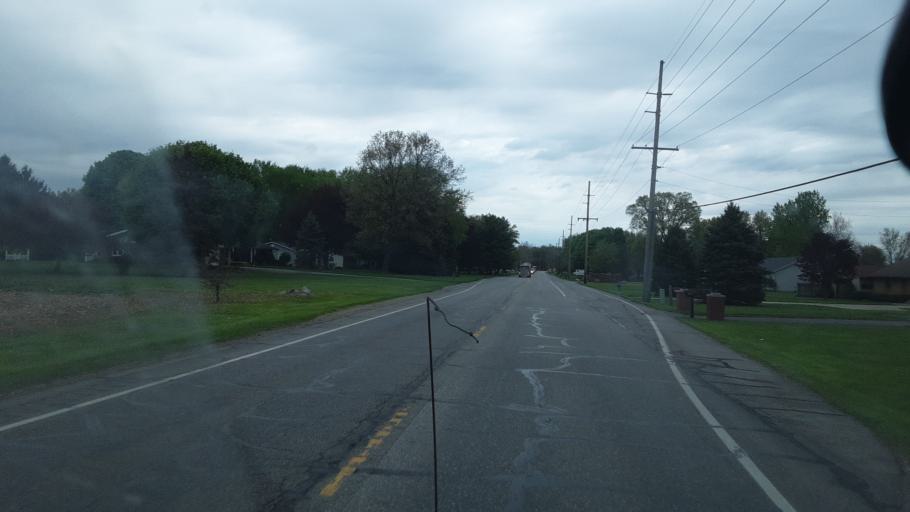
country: US
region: Indiana
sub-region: Elkhart County
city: Goshen
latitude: 41.6338
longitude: -85.8282
